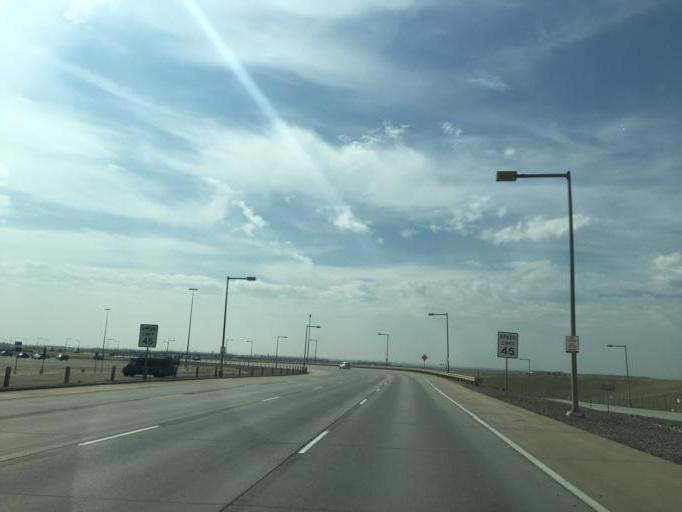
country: US
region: Colorado
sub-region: Weld County
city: Lochbuie
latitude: 39.8483
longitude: -104.6822
